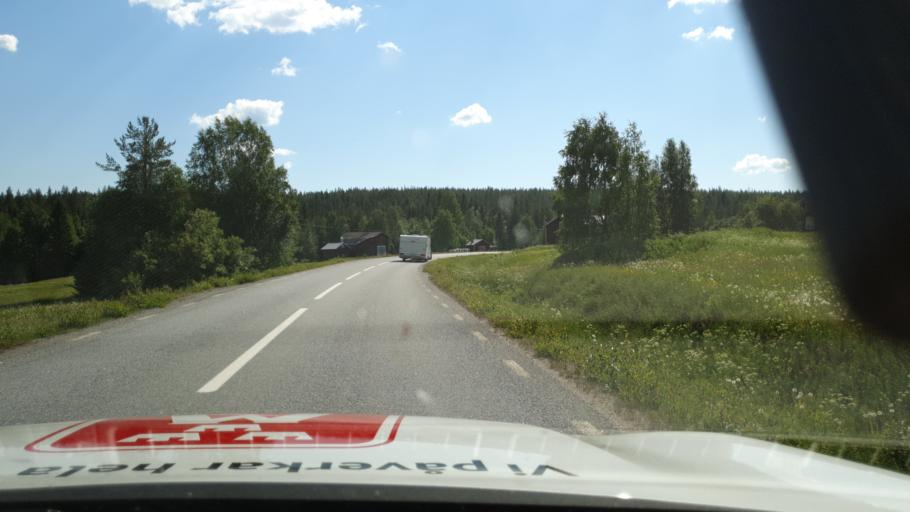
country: SE
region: Vaesterbotten
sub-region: Skelleftea Kommun
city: Burtraesk
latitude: 64.3804
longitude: 20.2684
